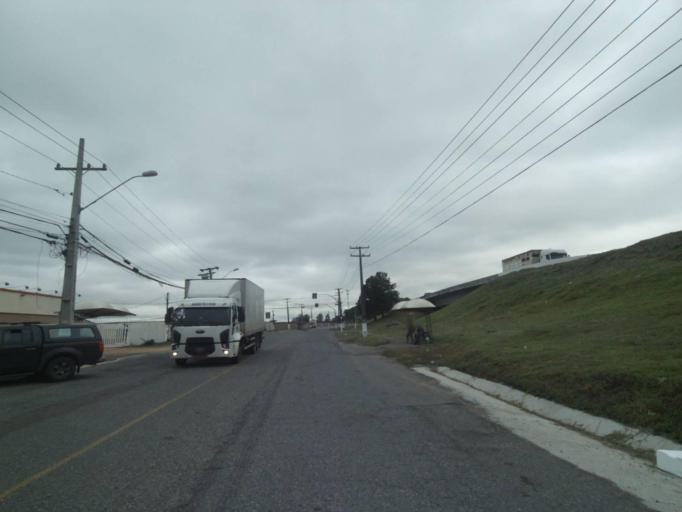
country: BR
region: Parana
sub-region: Sao Jose Dos Pinhais
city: Sao Jose dos Pinhais
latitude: -25.5339
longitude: -49.3174
